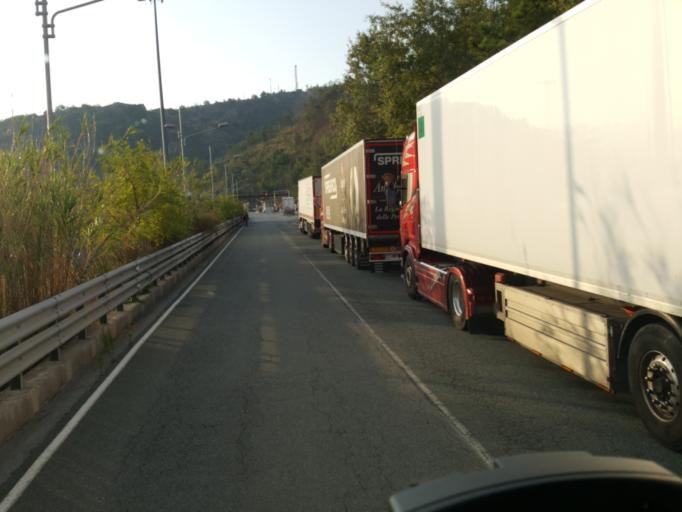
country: IT
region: Liguria
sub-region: Provincia di Savona
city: Vado Ligure
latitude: 44.2638
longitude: 8.4411
